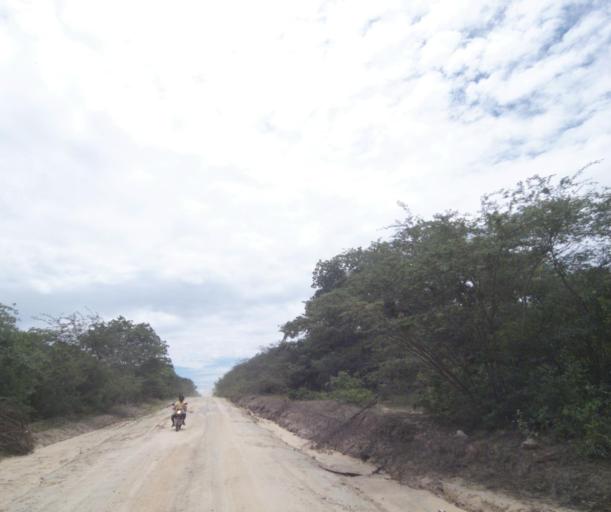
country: BR
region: Bahia
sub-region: Carinhanha
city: Carinhanha
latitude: -14.2131
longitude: -43.8963
